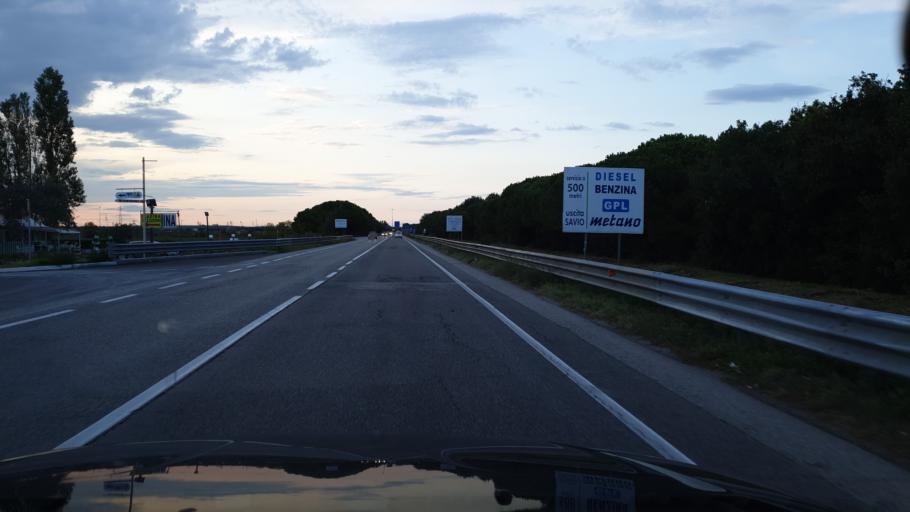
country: IT
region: Emilia-Romagna
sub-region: Provincia di Ravenna
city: Savio
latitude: 44.2836
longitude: 12.3155
